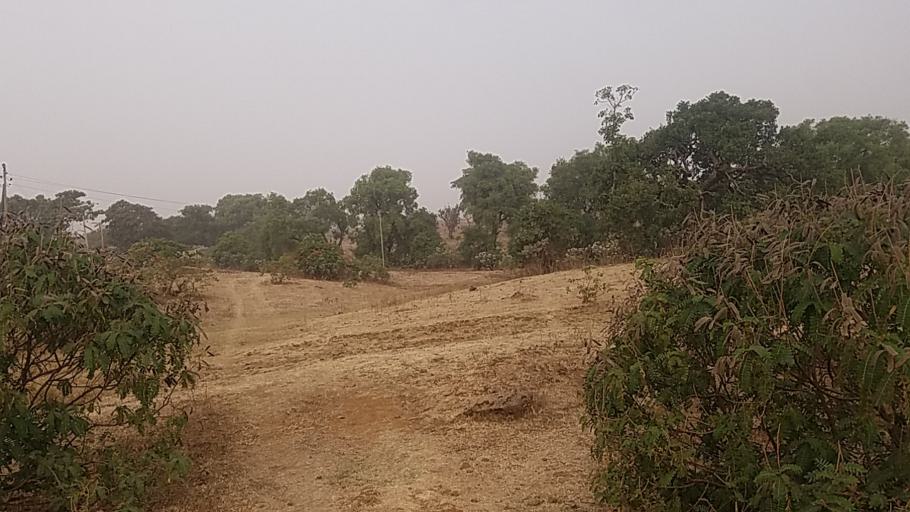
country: ET
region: Amhara
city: Bure
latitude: 10.9775
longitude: 36.4952
